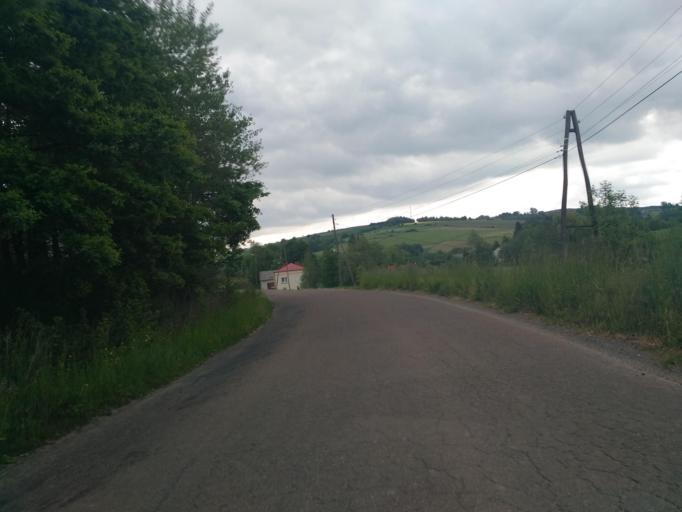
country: PL
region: Subcarpathian Voivodeship
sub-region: Powiat jasielski
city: Tarnowiec
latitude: 49.6784
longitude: 21.5889
